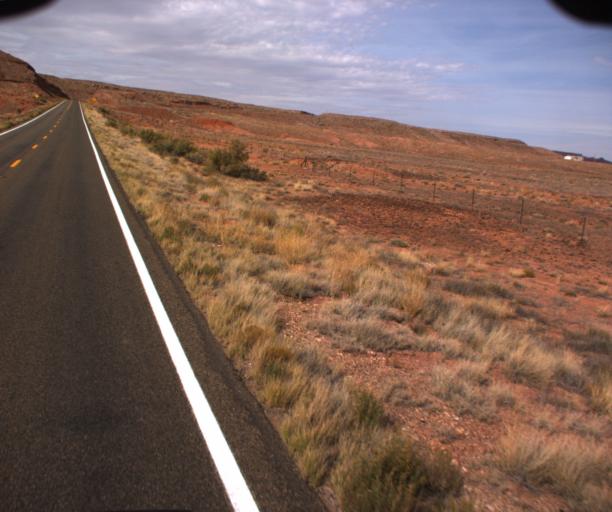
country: US
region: Arizona
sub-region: Apache County
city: Many Farms
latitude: 36.5419
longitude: -109.5249
